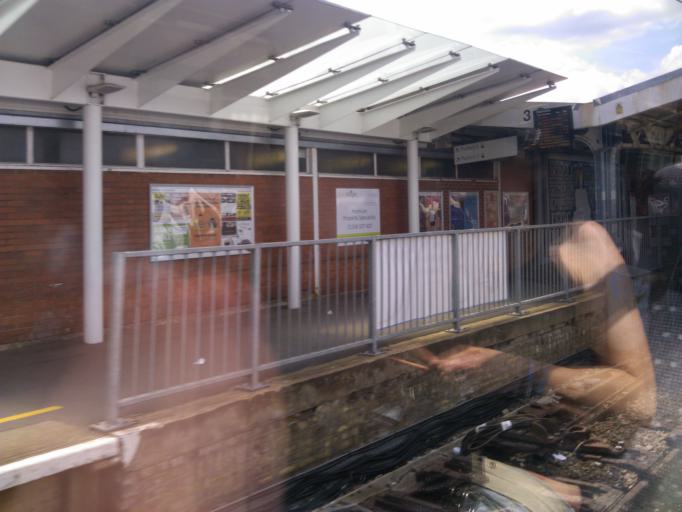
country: GB
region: England
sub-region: Essex
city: Colchester
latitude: 51.9005
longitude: 0.8923
